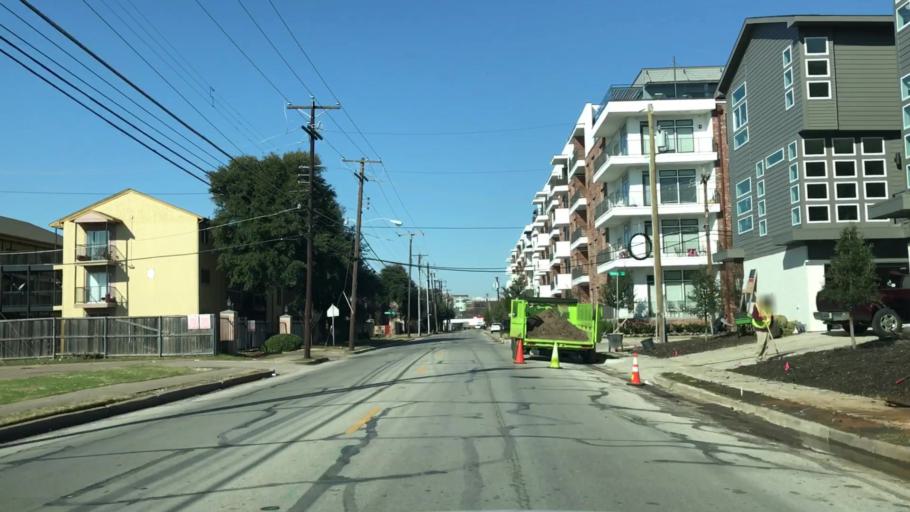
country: US
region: Texas
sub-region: Dallas County
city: Highland Park
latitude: 32.8128
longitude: -96.7839
